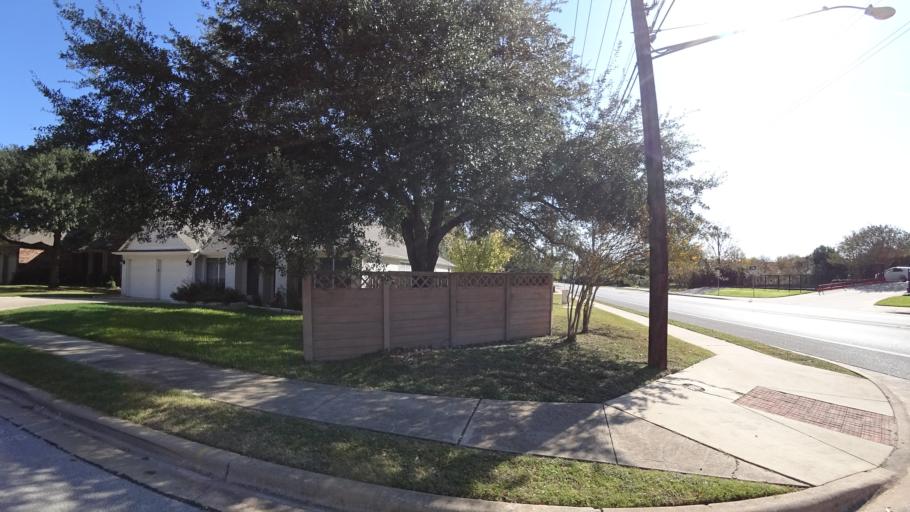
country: US
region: Texas
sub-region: Travis County
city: Shady Hollow
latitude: 30.2194
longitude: -97.8552
